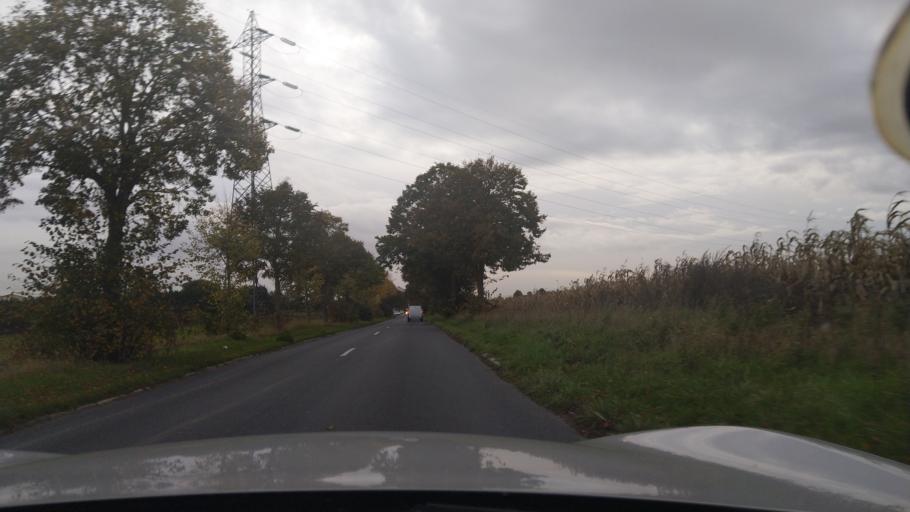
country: FR
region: Ile-de-France
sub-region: Departement de Seine-Saint-Denis
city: Villepinte
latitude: 48.9729
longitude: 2.5521
